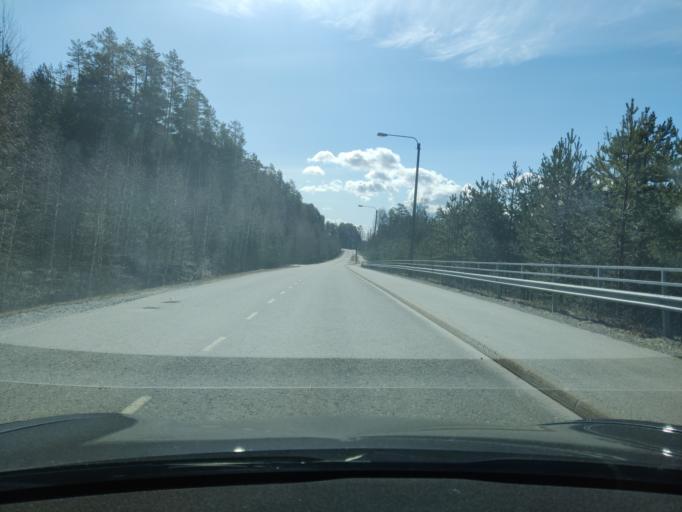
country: FI
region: Northern Savo
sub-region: Kuopio
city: Vehmersalmi
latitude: 62.7704
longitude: 28.0083
